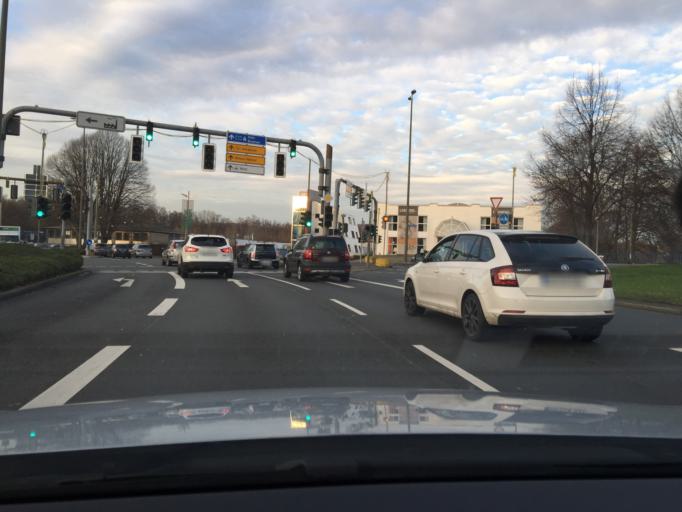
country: DE
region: North Rhine-Westphalia
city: Herdecke
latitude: 51.3844
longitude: 7.4491
